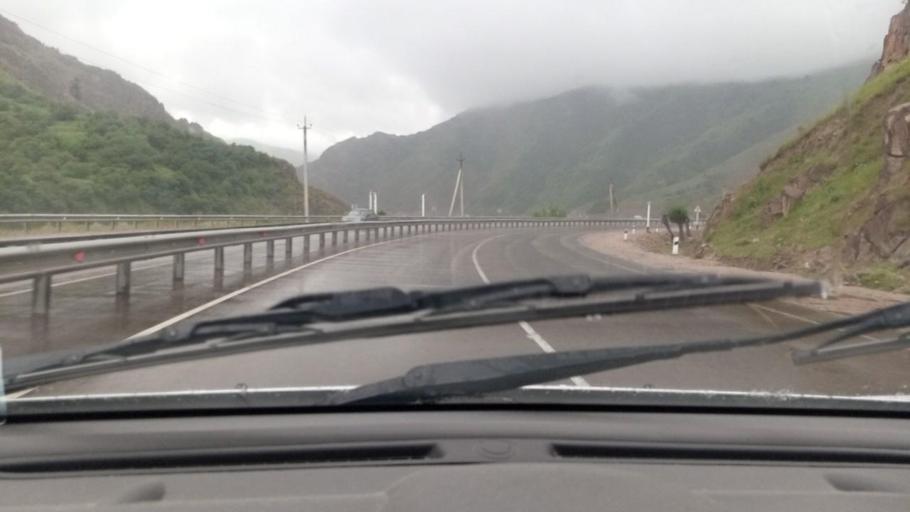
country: UZ
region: Toshkent
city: Angren
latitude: 41.1008
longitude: 70.3295
